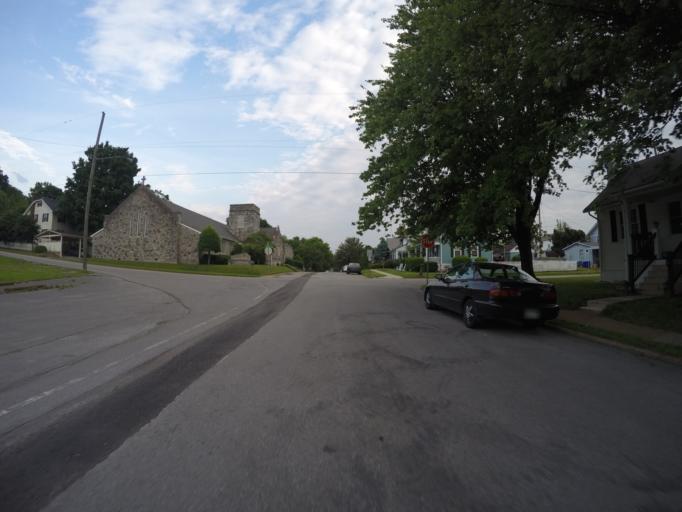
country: US
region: Tennessee
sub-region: Davidson County
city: Lakewood
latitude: 36.2632
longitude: -86.6454
